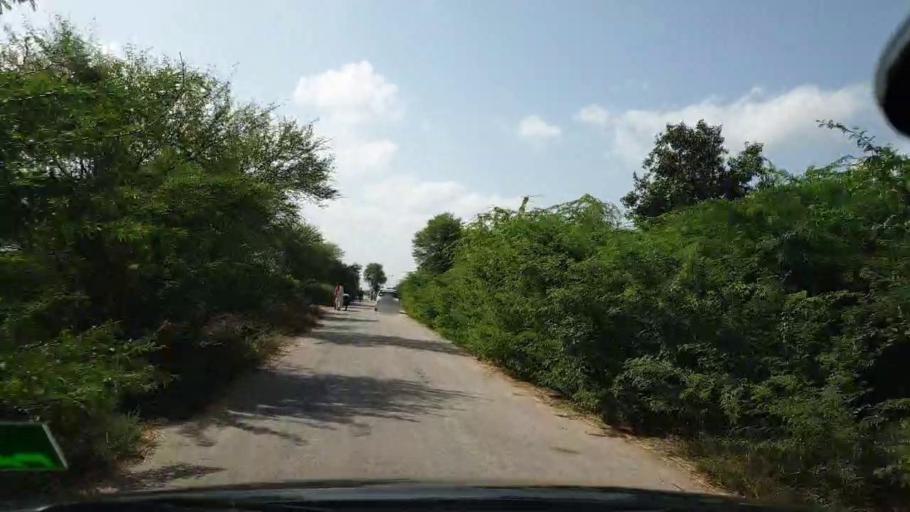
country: PK
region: Sindh
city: Kadhan
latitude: 24.6348
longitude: 69.1159
